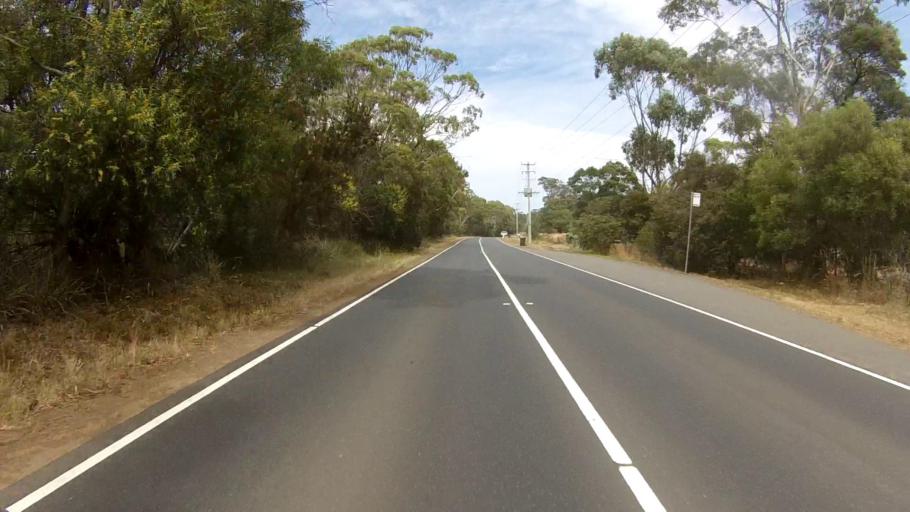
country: AU
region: Tasmania
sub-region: Clarence
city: Acton Park
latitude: -42.8751
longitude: 147.4829
